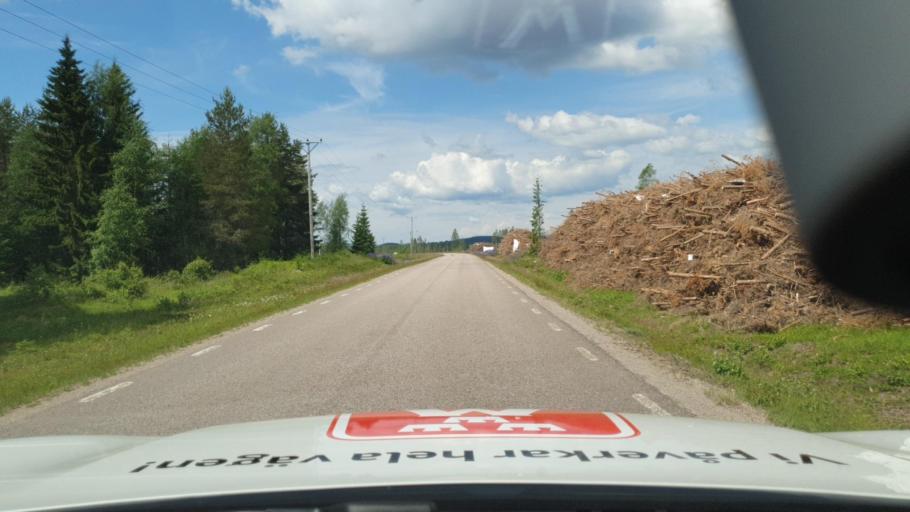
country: SE
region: Vaermland
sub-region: Torsby Kommun
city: Torsby
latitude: 60.5027
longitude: 12.8542
